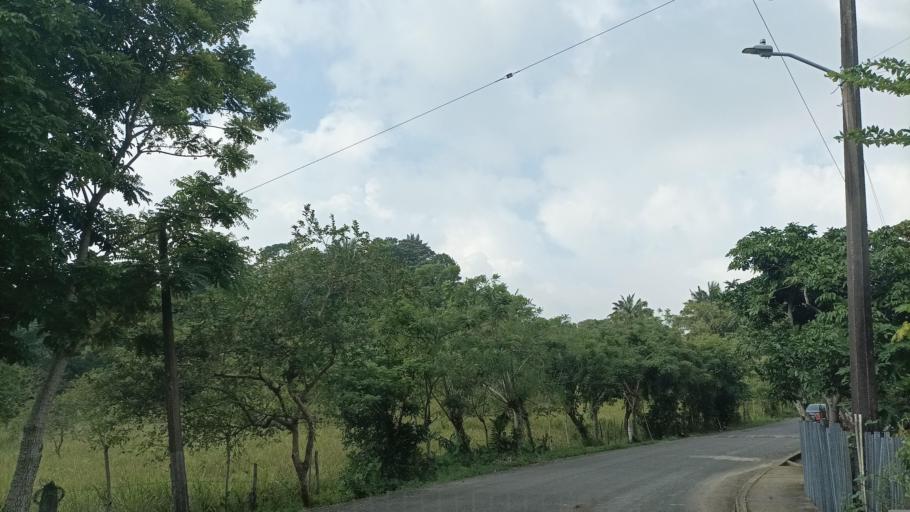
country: MX
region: Veracruz
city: Allende
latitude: 18.1271
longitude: -94.2838
